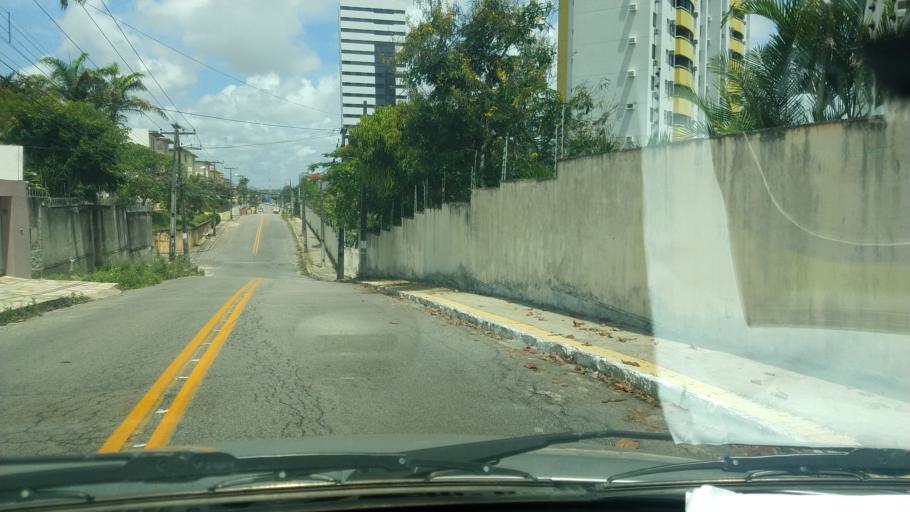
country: BR
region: Rio Grande do Norte
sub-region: Natal
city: Natal
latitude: -5.8646
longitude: -35.2003
